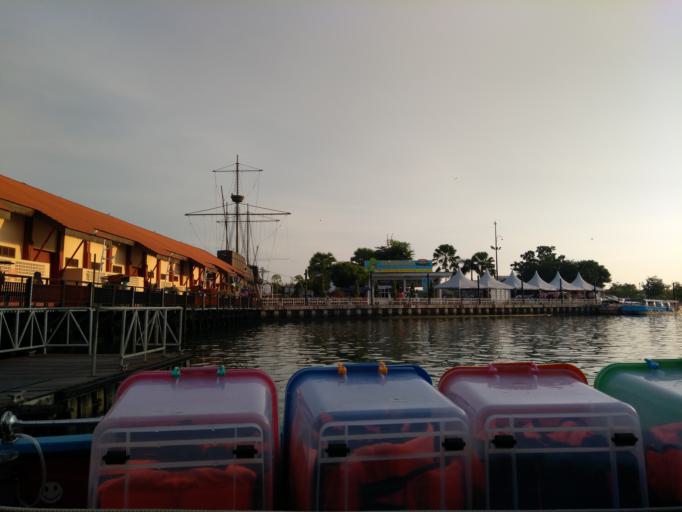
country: MY
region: Melaka
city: Malacca
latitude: 2.1931
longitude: 102.2471
